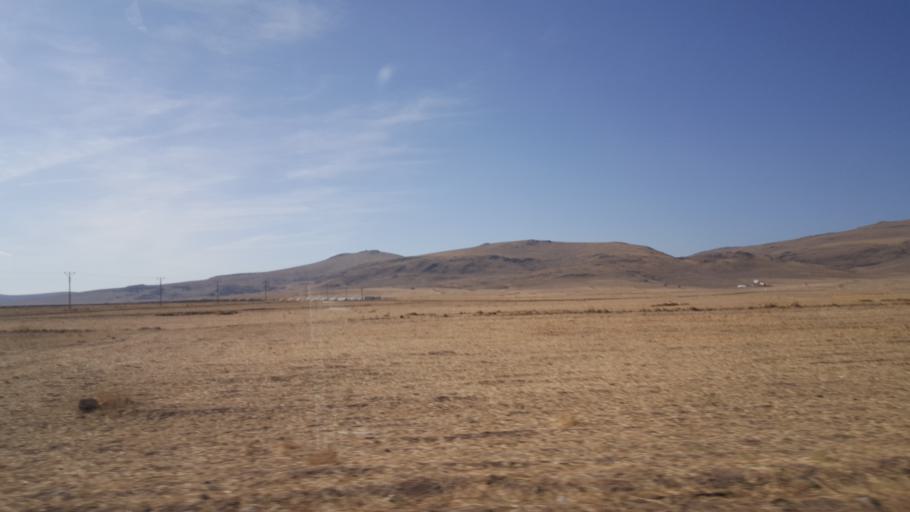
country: TR
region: Ankara
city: Altpinar
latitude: 39.2684
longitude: 32.7541
